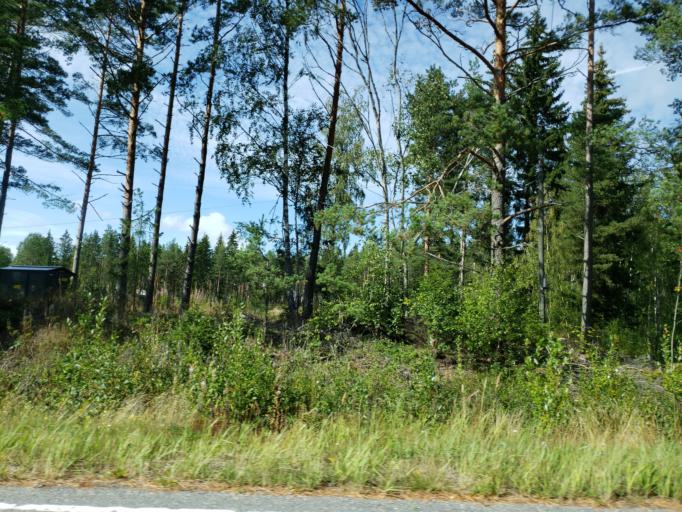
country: FI
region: Varsinais-Suomi
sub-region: Aboland-Turunmaa
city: Vaestanfjaerd
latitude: 60.1128
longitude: 22.6077
